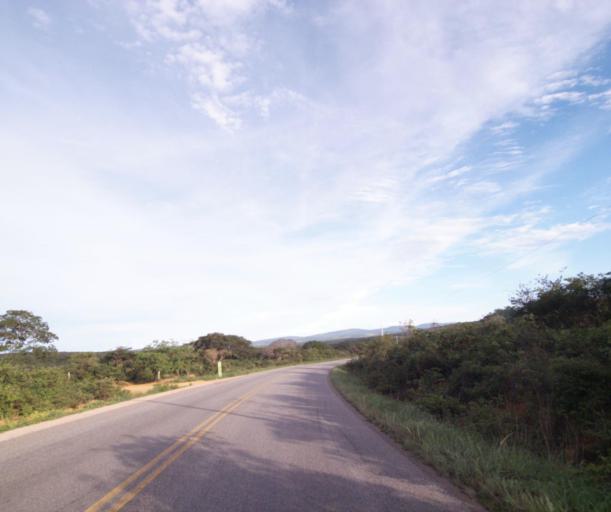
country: BR
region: Bahia
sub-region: Caetite
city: Caetite
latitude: -14.1673
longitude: -42.3002
